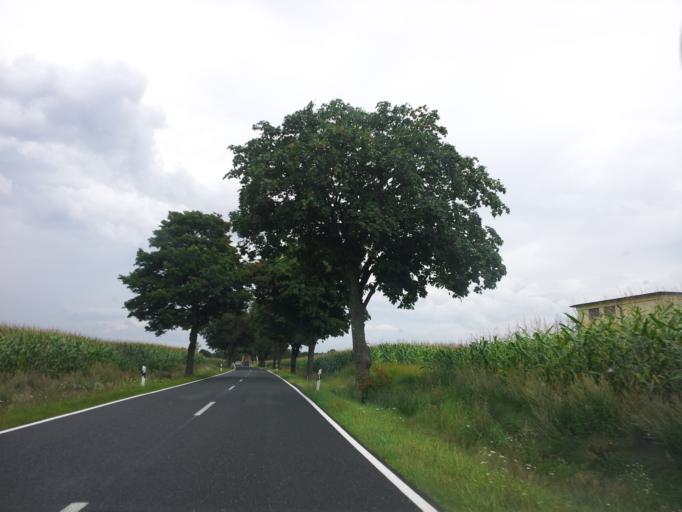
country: DE
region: Brandenburg
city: Gorzke
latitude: 52.1731
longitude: 12.3853
